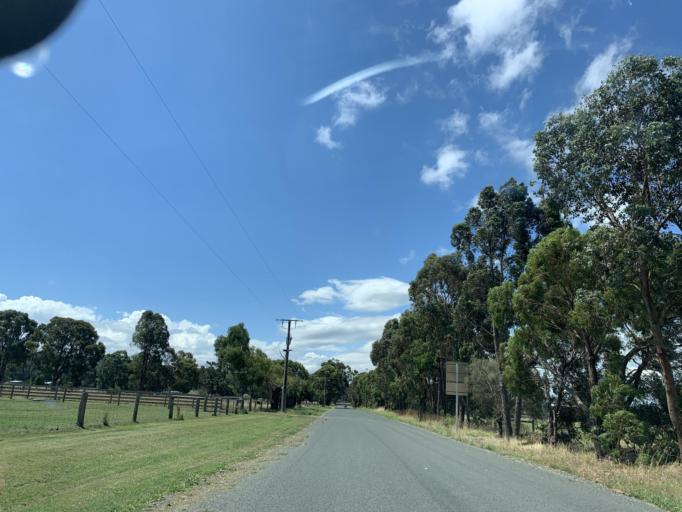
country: AU
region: Victoria
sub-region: Wellington
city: Heyfield
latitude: -38.0099
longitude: 146.6530
